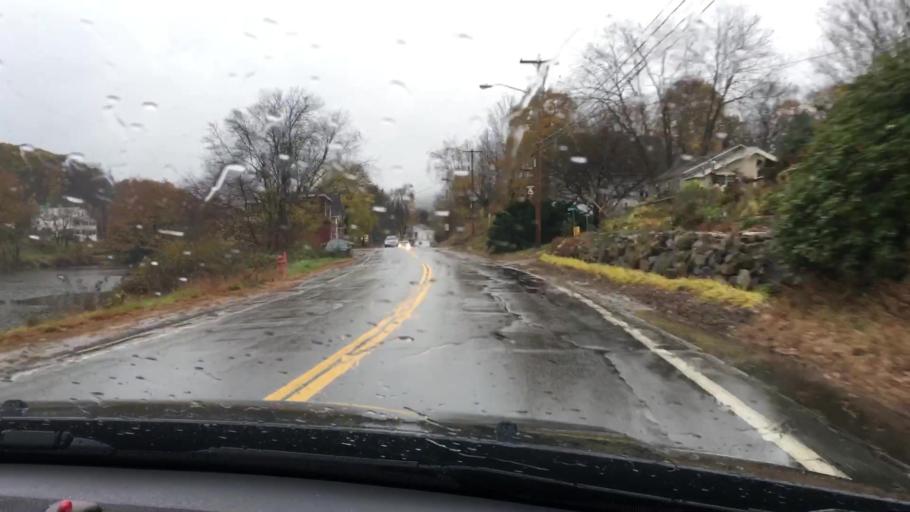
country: US
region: New Hampshire
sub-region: Grafton County
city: Ashland
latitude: 43.6983
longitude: -71.6306
